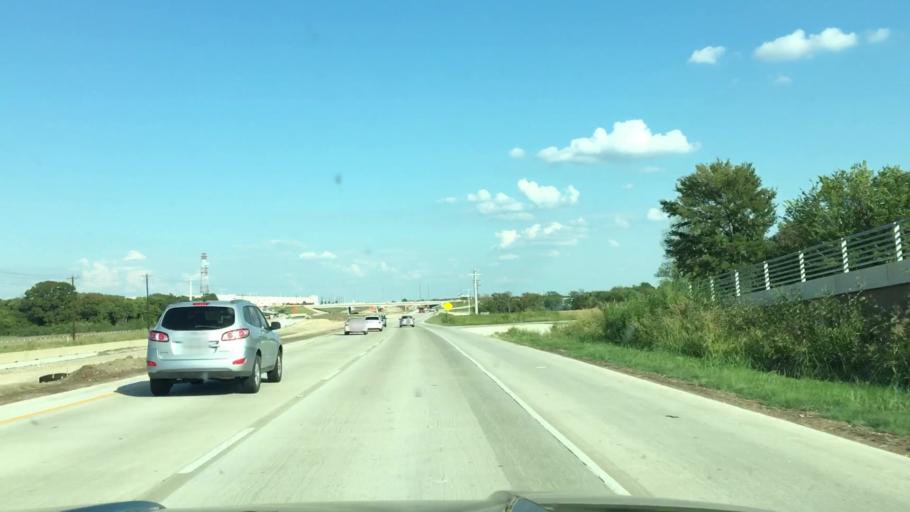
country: US
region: Texas
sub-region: Denton County
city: Justin
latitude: 33.0330
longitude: -97.3170
